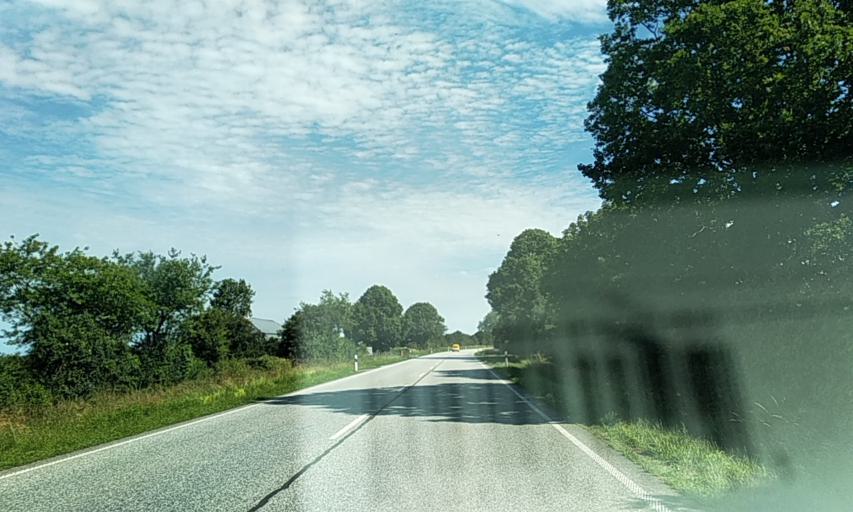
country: DE
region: Schleswig-Holstein
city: Jagel
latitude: 54.4376
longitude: 9.5335
